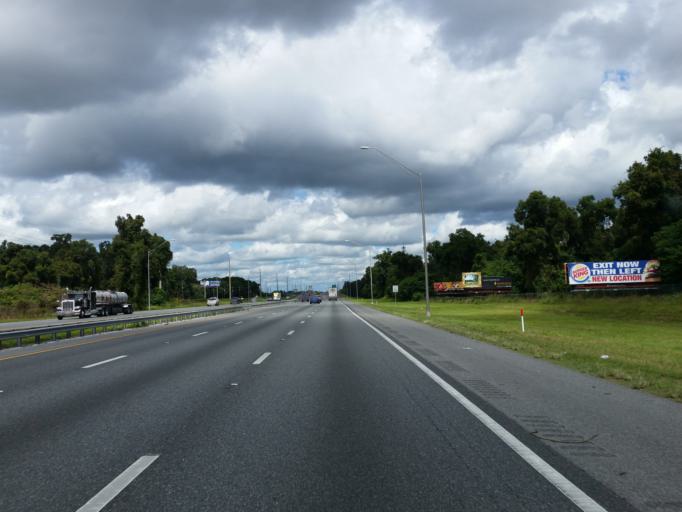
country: US
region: Florida
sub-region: Marion County
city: Ocala
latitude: 29.1592
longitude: -82.1848
